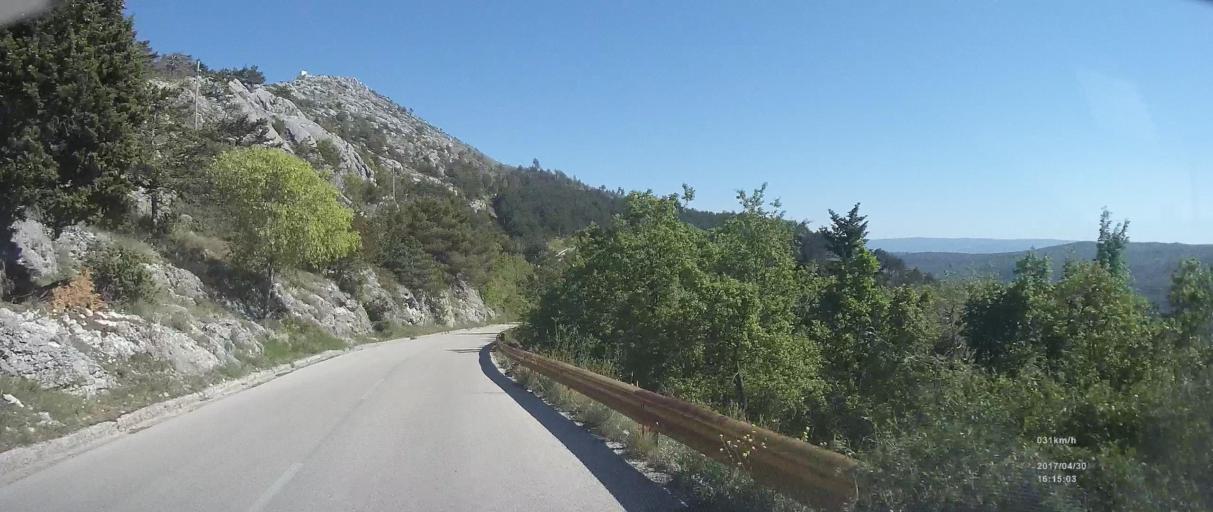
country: HR
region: Splitsko-Dalmatinska
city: Srinjine
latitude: 43.5101
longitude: 16.6051
